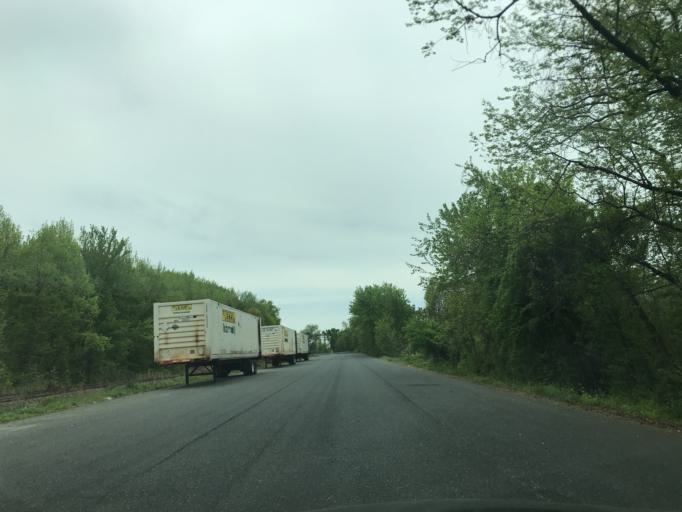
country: US
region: Maryland
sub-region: Baltimore County
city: Edgemere
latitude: 39.2489
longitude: -76.4682
